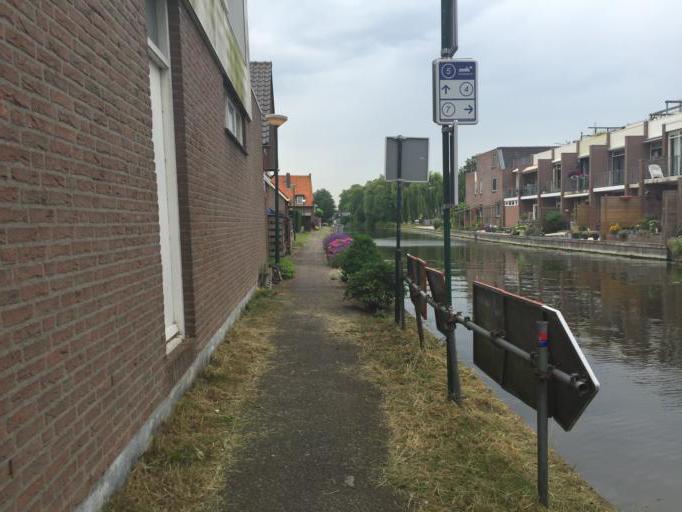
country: NL
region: Utrecht
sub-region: Gemeente Woerden
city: Woerden
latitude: 52.0864
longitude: 4.8617
